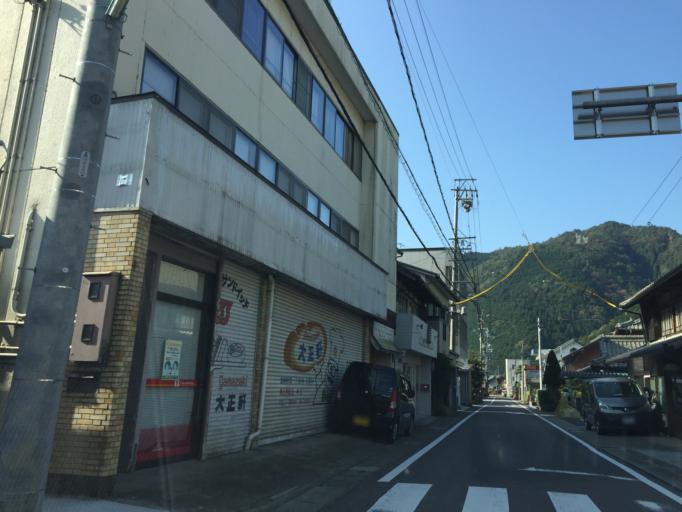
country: JP
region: Gifu
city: Minokamo
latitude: 35.5436
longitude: 137.1207
